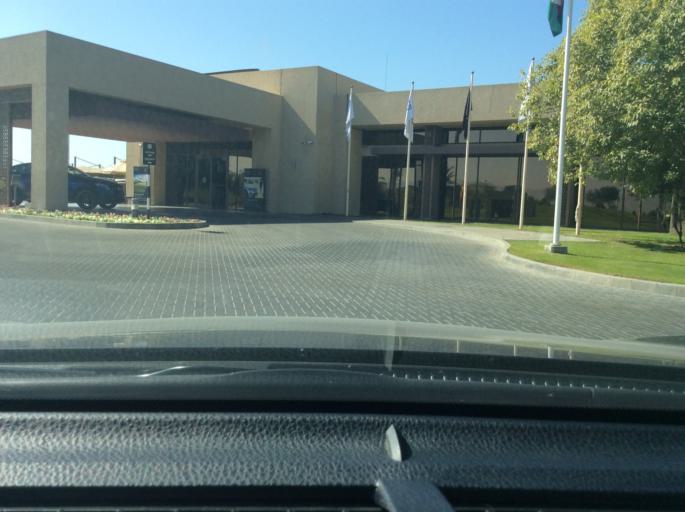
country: OM
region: Muhafazat Masqat
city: Bawshar
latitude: 23.6126
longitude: 58.3024
